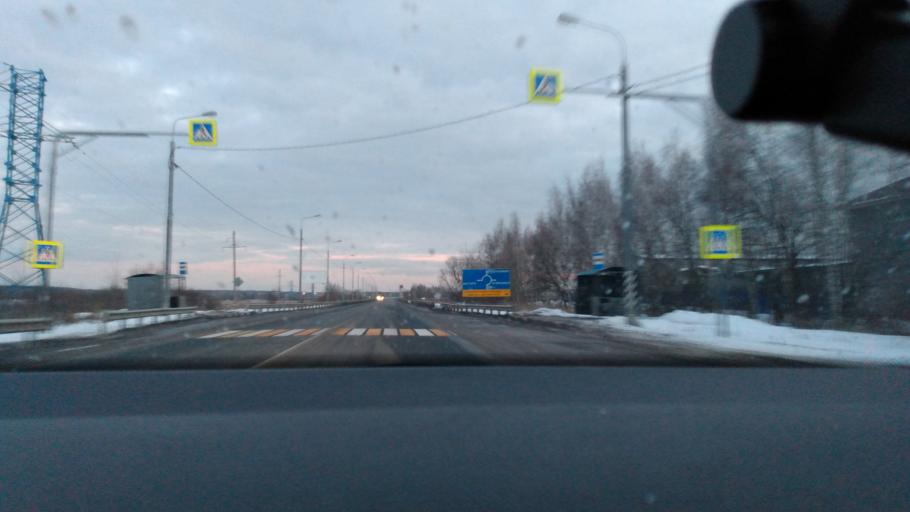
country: RU
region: Moskovskaya
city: Yegor'yevsk
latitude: 55.3931
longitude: 39.0718
